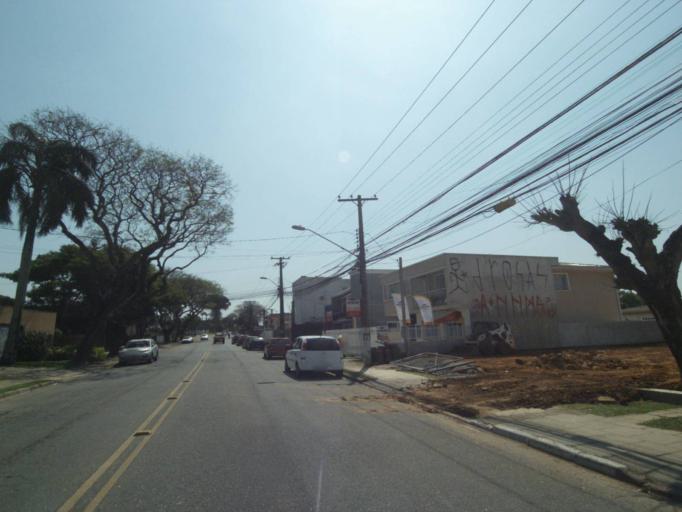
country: BR
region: Parana
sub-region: Curitiba
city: Curitiba
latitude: -25.4773
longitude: -49.3133
